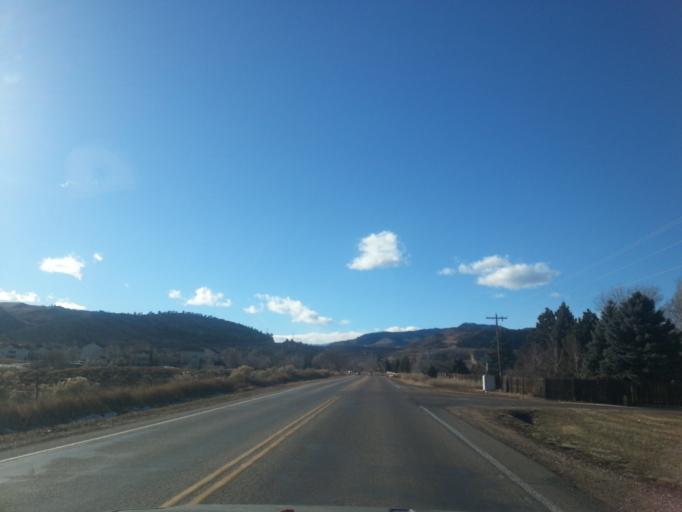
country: US
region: Colorado
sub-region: Larimer County
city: Fort Collins
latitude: 40.5309
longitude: -105.1225
